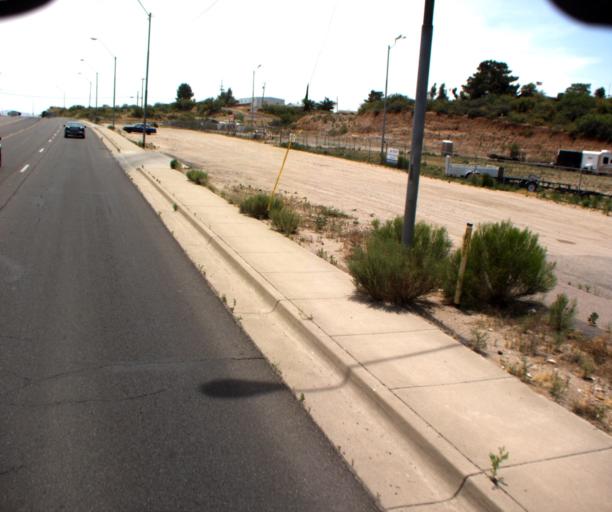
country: US
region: Arizona
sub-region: Gila County
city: Globe
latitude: 33.3852
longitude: -110.7579
